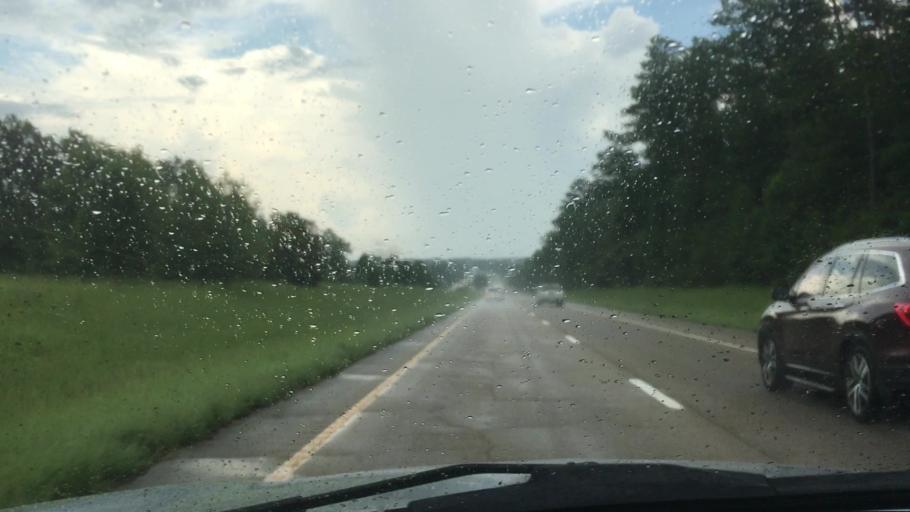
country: US
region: Mississippi
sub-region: Lamar County
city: Purvis
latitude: 31.1597
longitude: -89.3572
